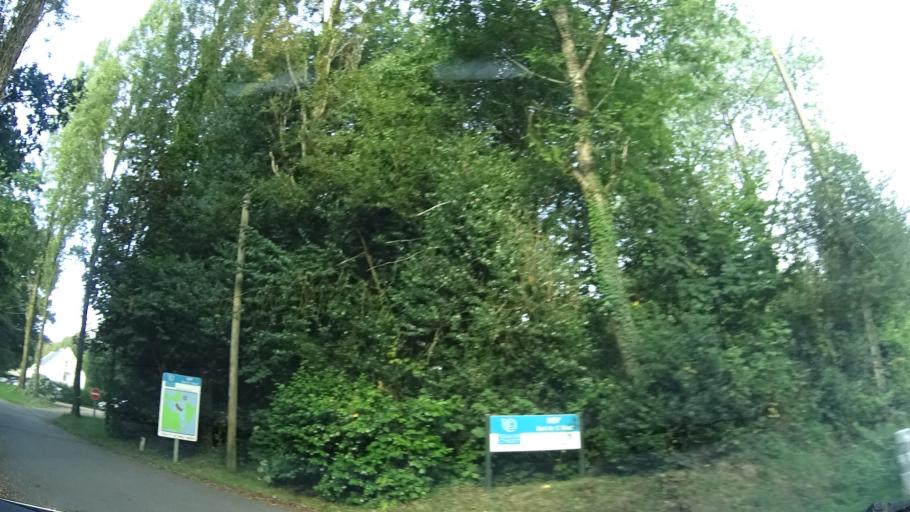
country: FR
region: Brittany
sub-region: Departement du Finistere
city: Chateaulin
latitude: 48.1977
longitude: -4.1065
